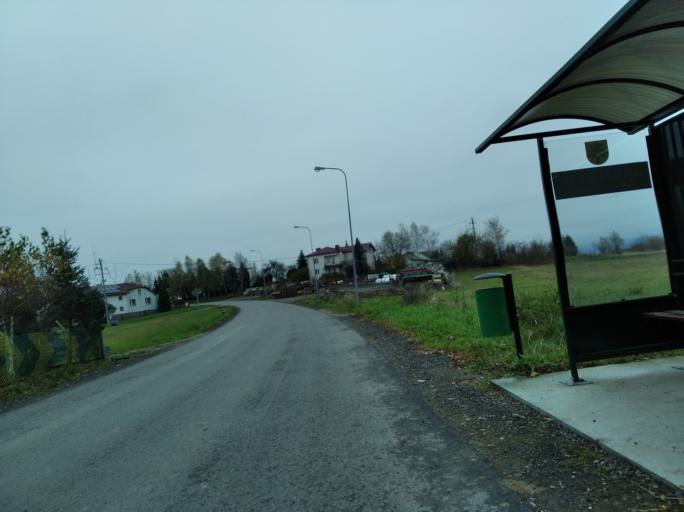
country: PL
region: Subcarpathian Voivodeship
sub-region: Powiat krosnienski
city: Jedlicze
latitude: 49.7287
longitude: 21.6527
